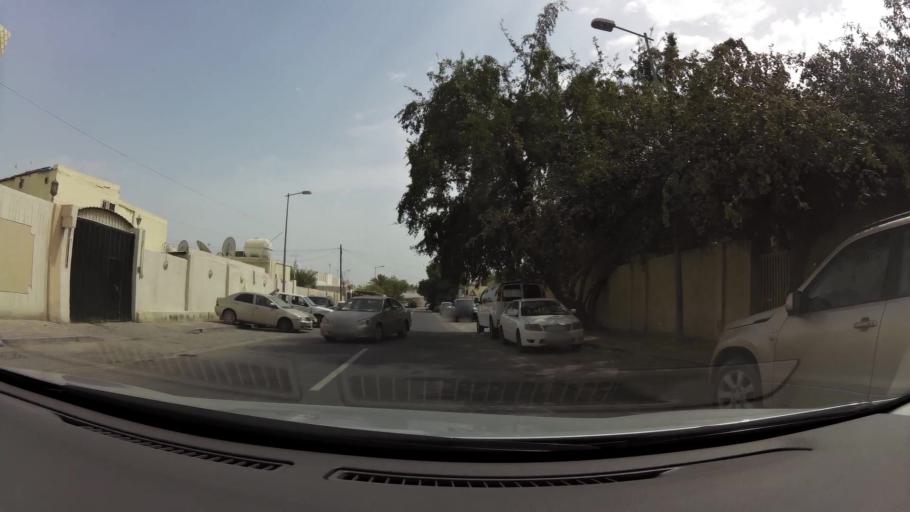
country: QA
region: Baladiyat ad Dawhah
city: Doha
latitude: 25.3118
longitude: 51.4832
